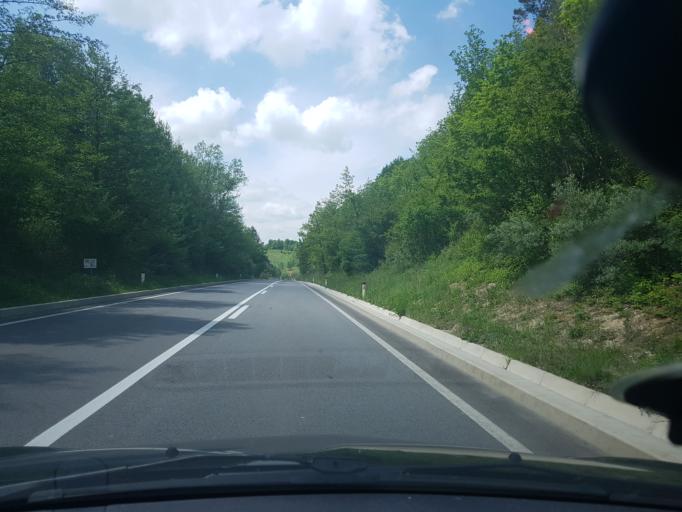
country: SI
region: Rogaska Slatina
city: Rogaska Slatina
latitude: 46.2420
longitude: 15.6629
